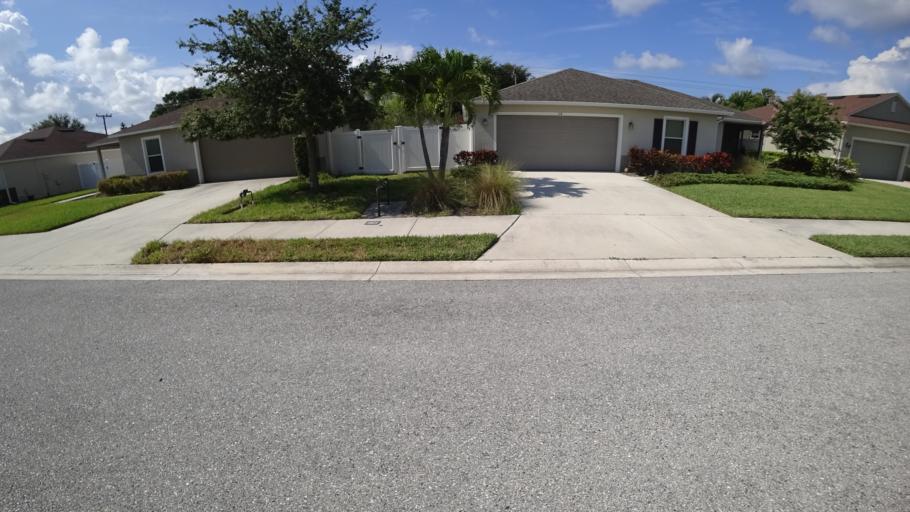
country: US
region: Florida
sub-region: Manatee County
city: Whitfield
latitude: 27.4261
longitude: -82.5620
